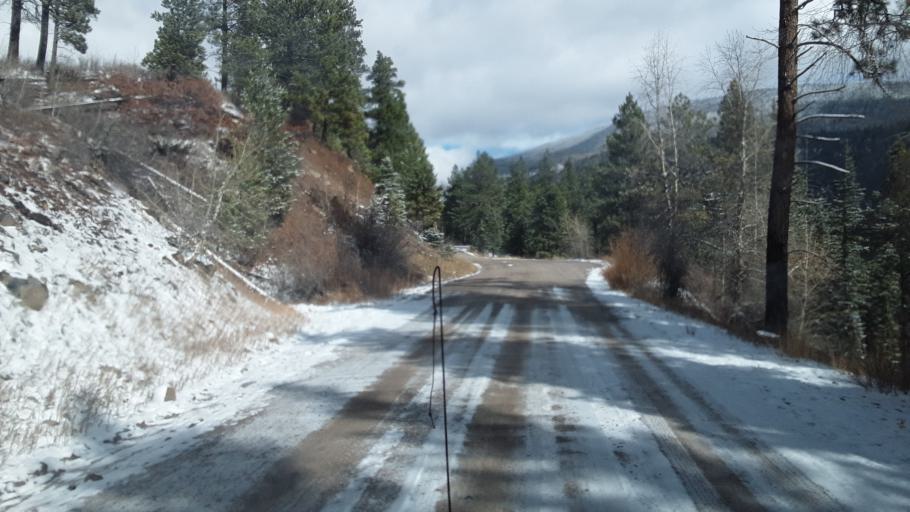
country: US
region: Colorado
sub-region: La Plata County
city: Bayfield
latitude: 37.4149
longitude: -107.5148
